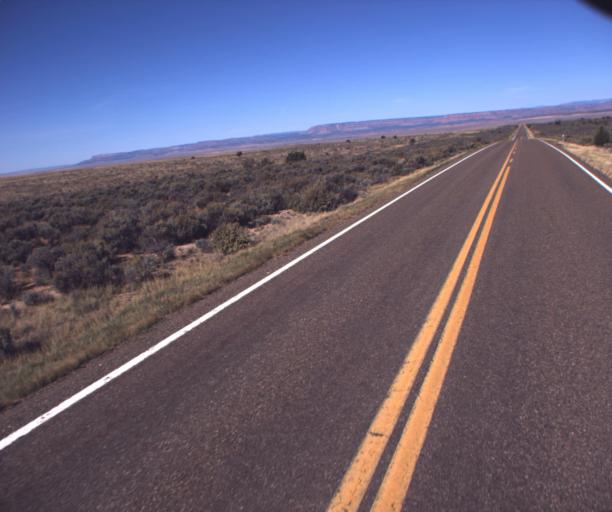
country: US
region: Arizona
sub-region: Coconino County
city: Fredonia
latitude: 36.8603
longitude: -112.3101
